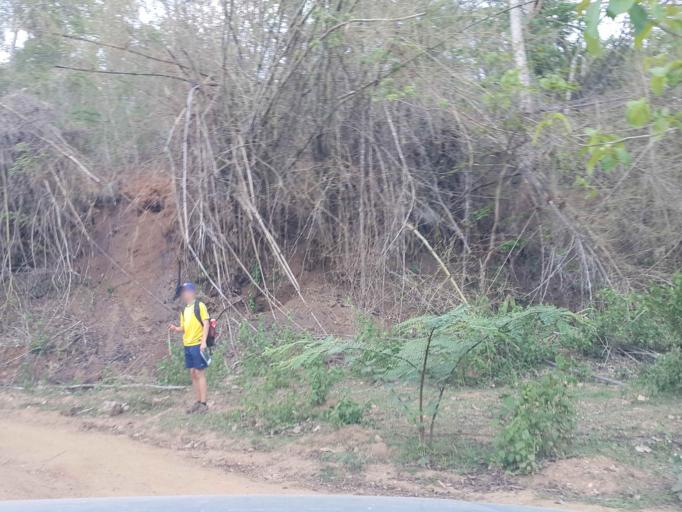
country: TH
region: Chiang Mai
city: Wiang Haeng
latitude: 19.3662
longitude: 98.7181
